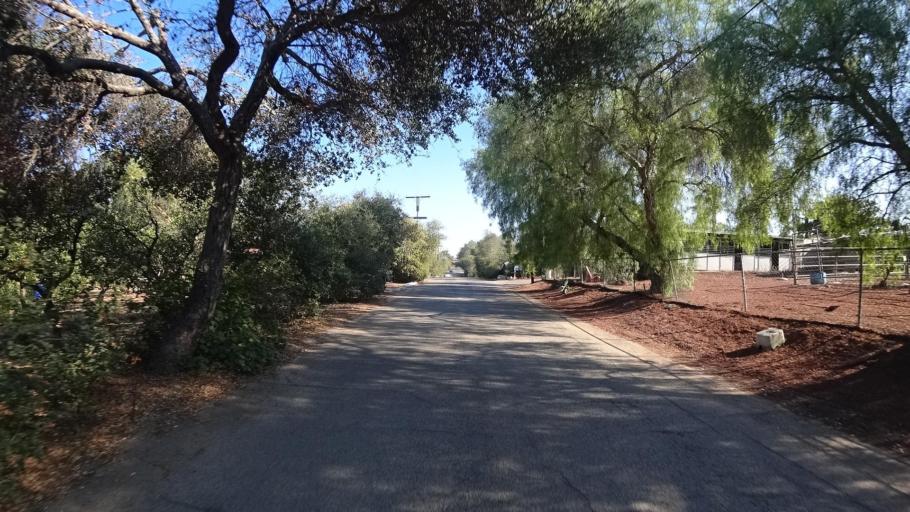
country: US
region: California
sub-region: San Diego County
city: Fallbrook
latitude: 33.3272
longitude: -117.2601
